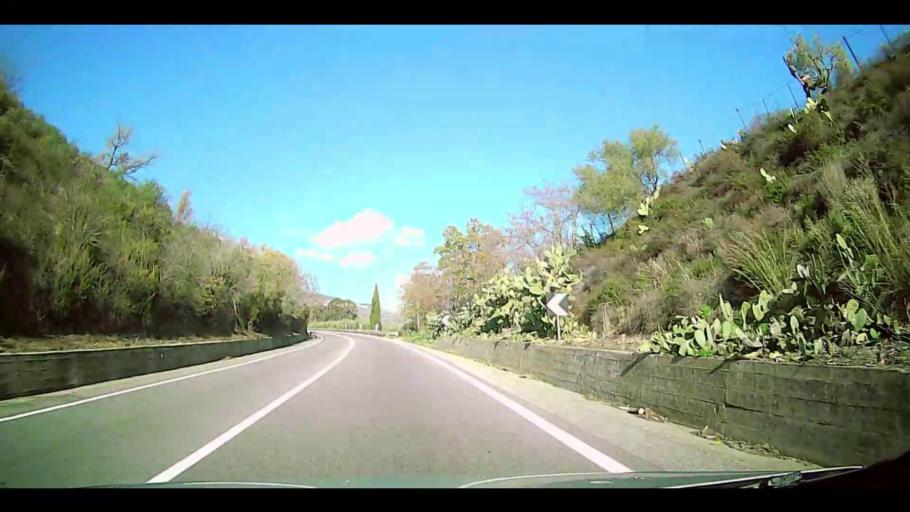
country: IT
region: Calabria
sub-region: Provincia di Crotone
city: Caccuri
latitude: 39.2015
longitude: 16.8111
